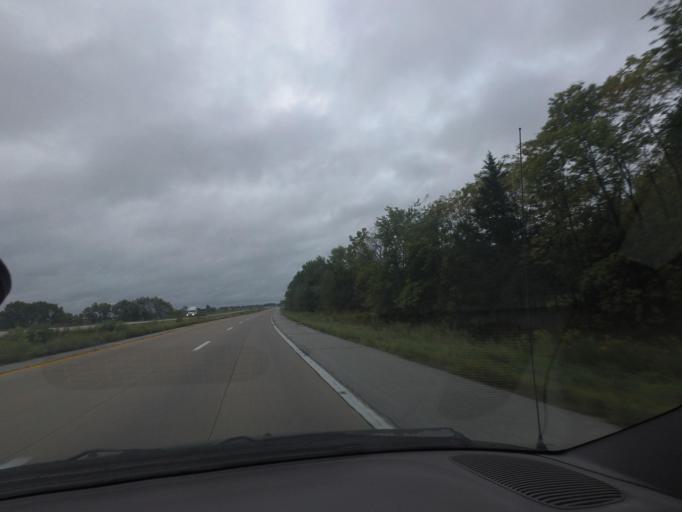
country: US
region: Missouri
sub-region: Marion County
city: Monroe City
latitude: 39.6717
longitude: -91.8574
